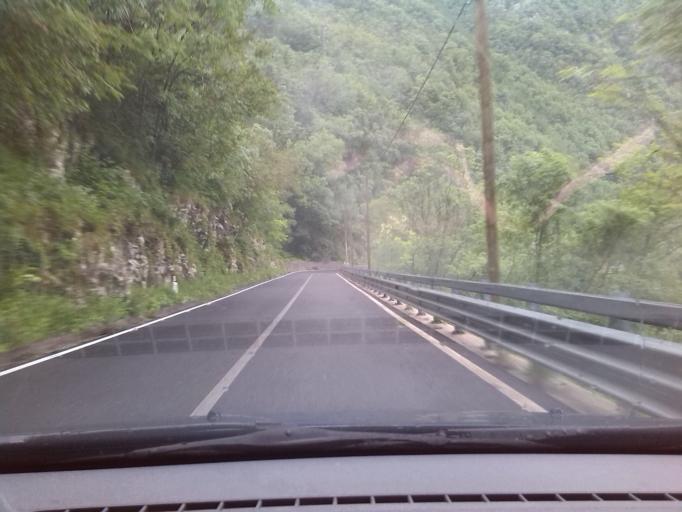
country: IT
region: Friuli Venezia Giulia
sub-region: Provincia di Udine
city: Lusevera
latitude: 46.2448
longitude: 13.2440
